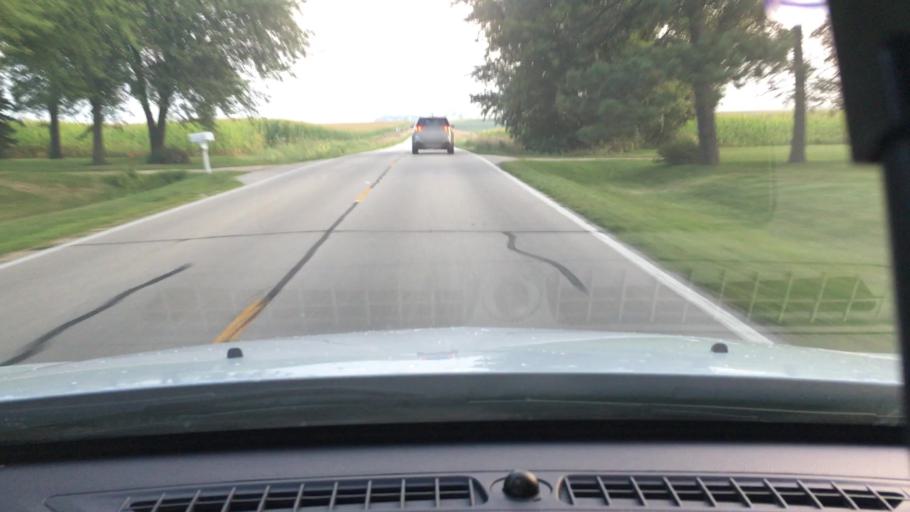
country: US
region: Illinois
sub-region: DeKalb County
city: Malta
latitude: 41.8500
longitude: -88.8478
